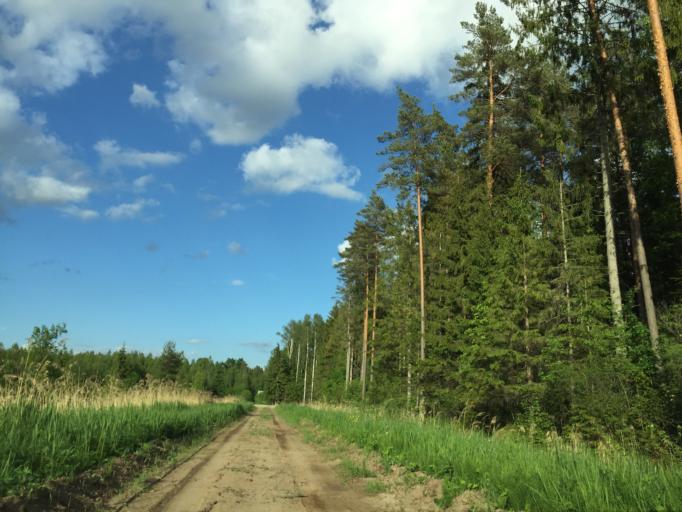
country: LV
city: Tireli
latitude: 56.7798
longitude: 23.4268
